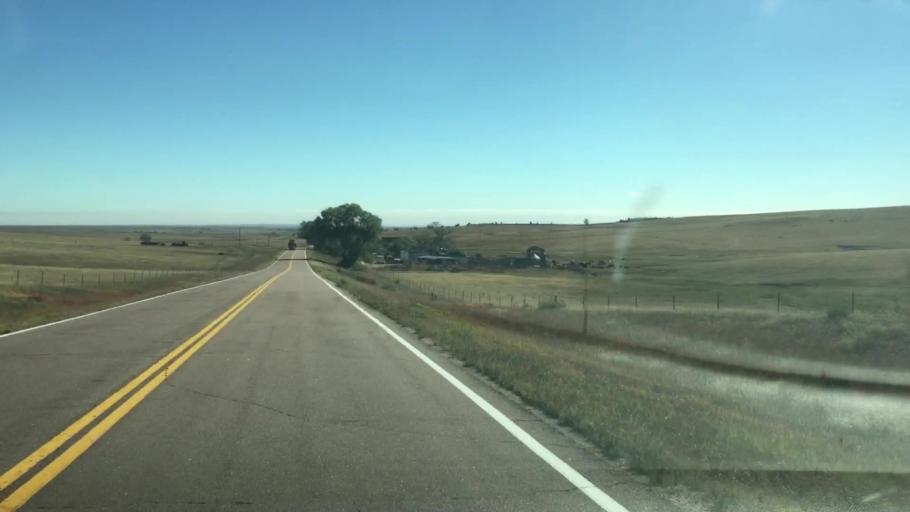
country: US
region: Colorado
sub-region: Lincoln County
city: Limon
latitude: 39.2882
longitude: -103.9641
